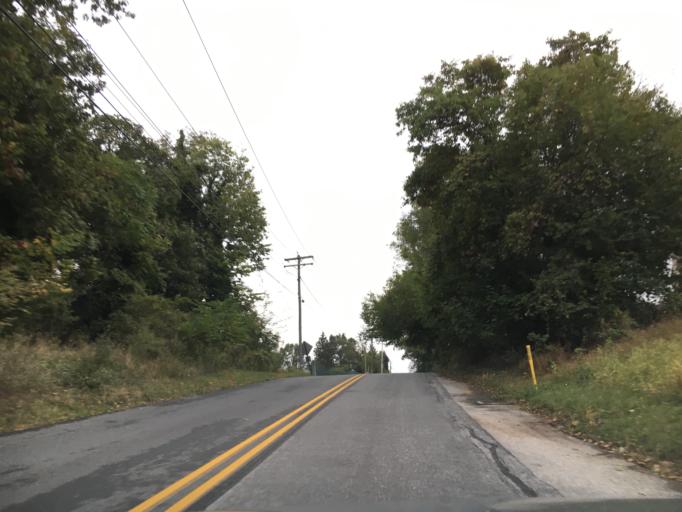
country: US
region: Pennsylvania
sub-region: York County
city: Grantley
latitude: 39.9327
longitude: -76.7156
